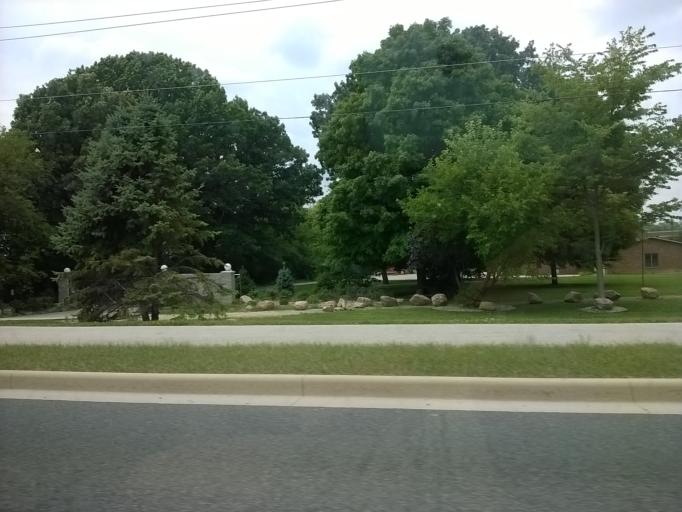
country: US
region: Indiana
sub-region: Hamilton County
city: Carmel
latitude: 39.9306
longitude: -86.0888
